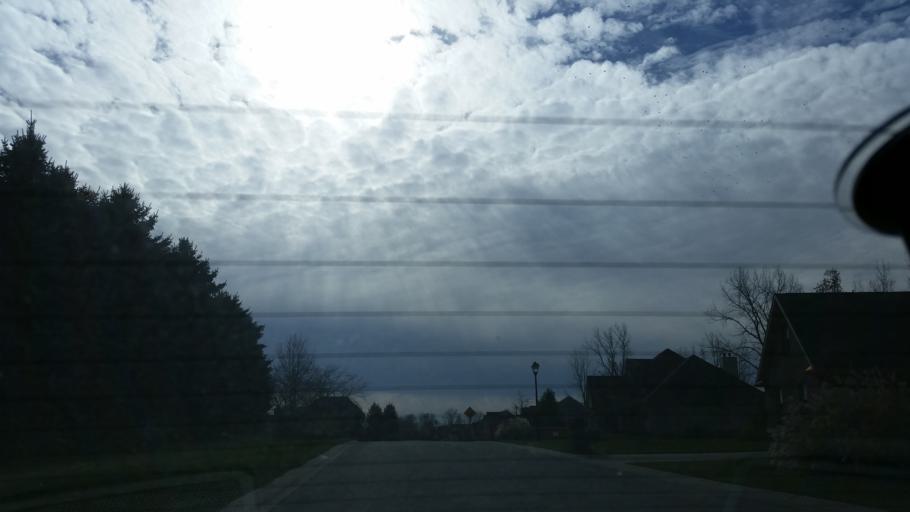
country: US
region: Indiana
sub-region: Howard County
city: Indian Heights
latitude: 40.4319
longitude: -86.1569
